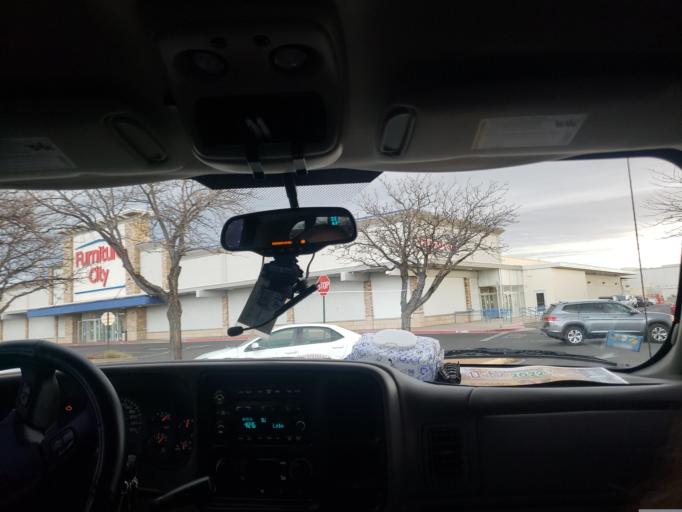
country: US
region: New Mexico
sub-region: Bernalillo County
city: North Valley
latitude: 35.1093
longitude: -106.5719
